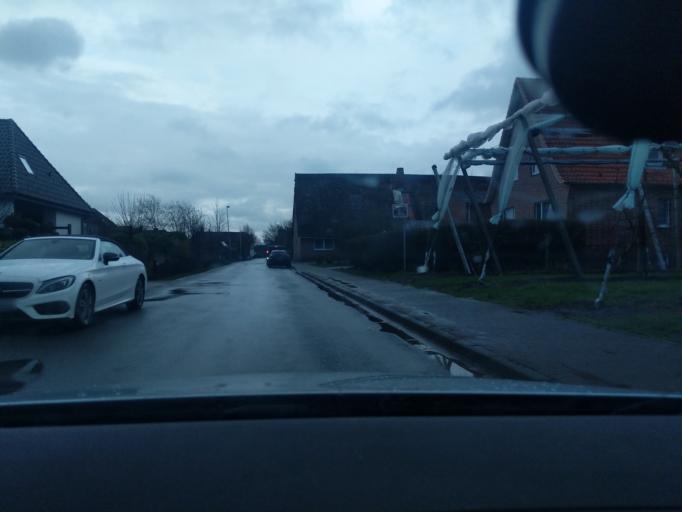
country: DE
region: Lower Saxony
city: Mittelnkirchen
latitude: 53.5244
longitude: 9.6466
